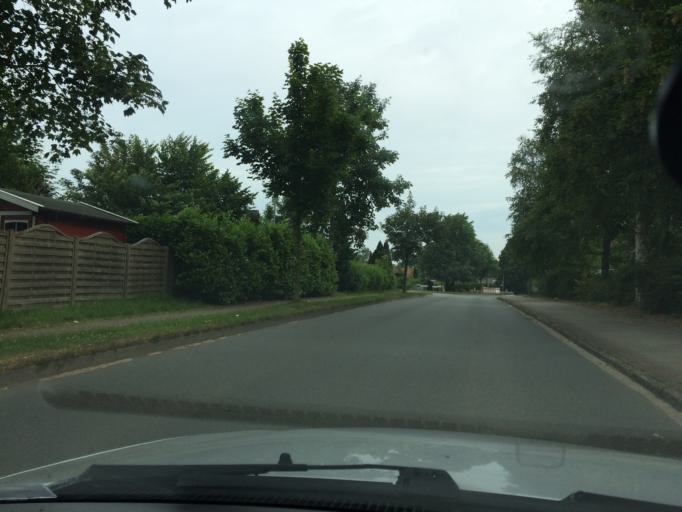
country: DE
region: Schleswig-Holstein
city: Oeversee
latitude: 54.6999
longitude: 9.4294
